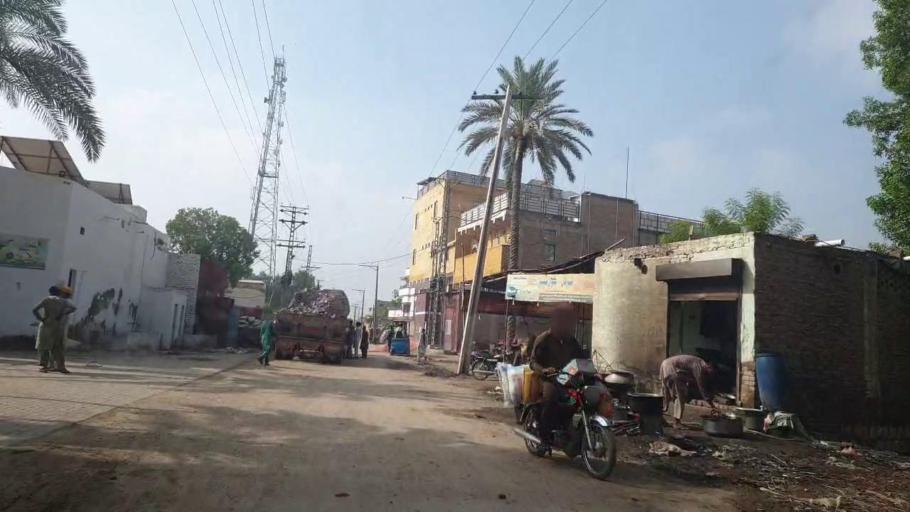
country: PK
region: Sindh
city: Khairpur
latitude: 27.5925
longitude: 68.7785
